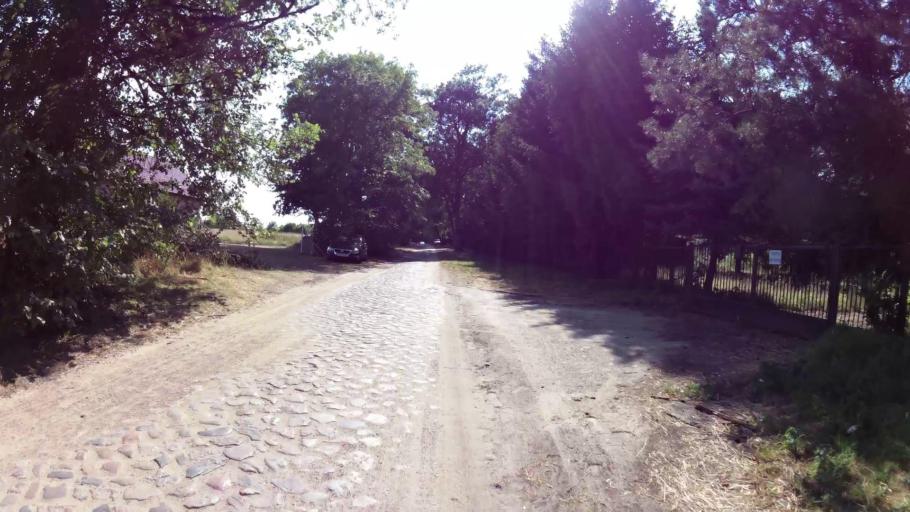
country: PL
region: West Pomeranian Voivodeship
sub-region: Powiat gryfinski
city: Moryn
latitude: 52.8589
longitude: 14.4232
